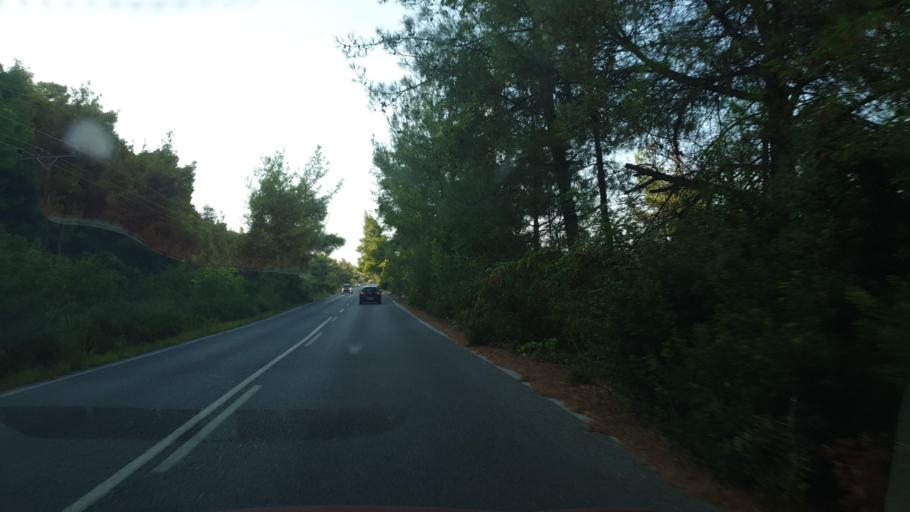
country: GR
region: Central Macedonia
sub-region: Nomos Chalkidikis
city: Agios Nikolaos
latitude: 40.2050
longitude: 23.7615
